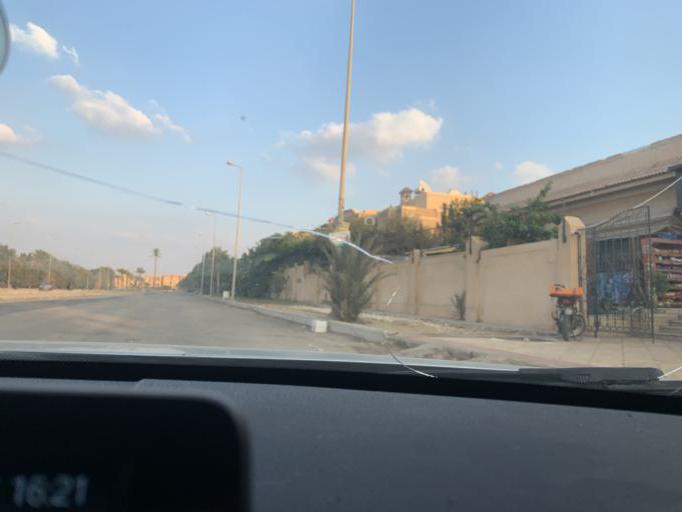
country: EG
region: Muhafazat al Qalyubiyah
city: Al Khankah
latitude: 30.0163
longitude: 31.4823
